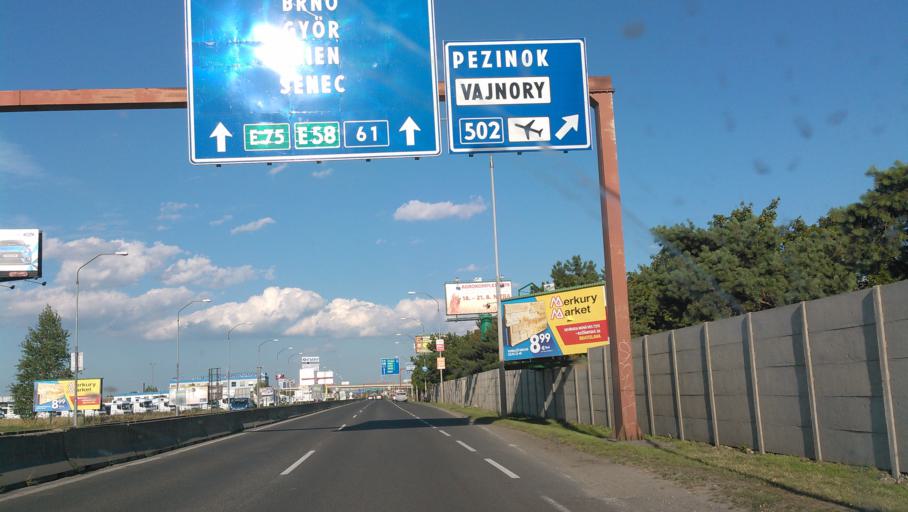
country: SK
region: Bratislavsky
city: Svaty Jur
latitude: 48.1895
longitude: 17.1932
